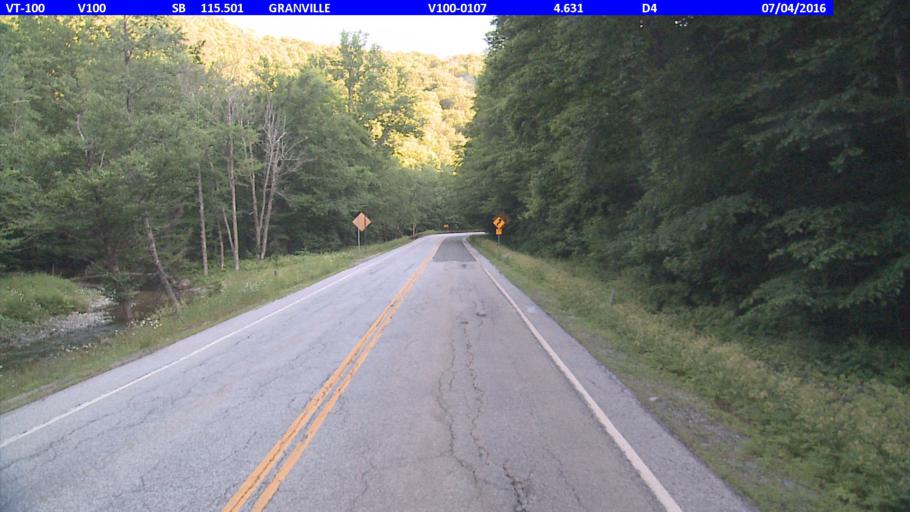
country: US
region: Vermont
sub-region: Orange County
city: Randolph
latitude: 44.0056
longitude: -72.8488
